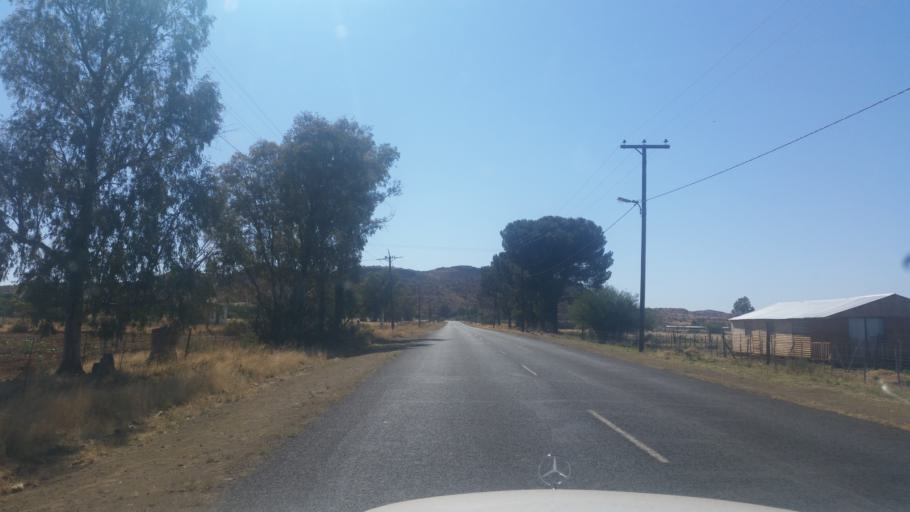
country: ZA
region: Orange Free State
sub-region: Xhariep District Municipality
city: Trompsburg
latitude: -30.4961
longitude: 25.9919
